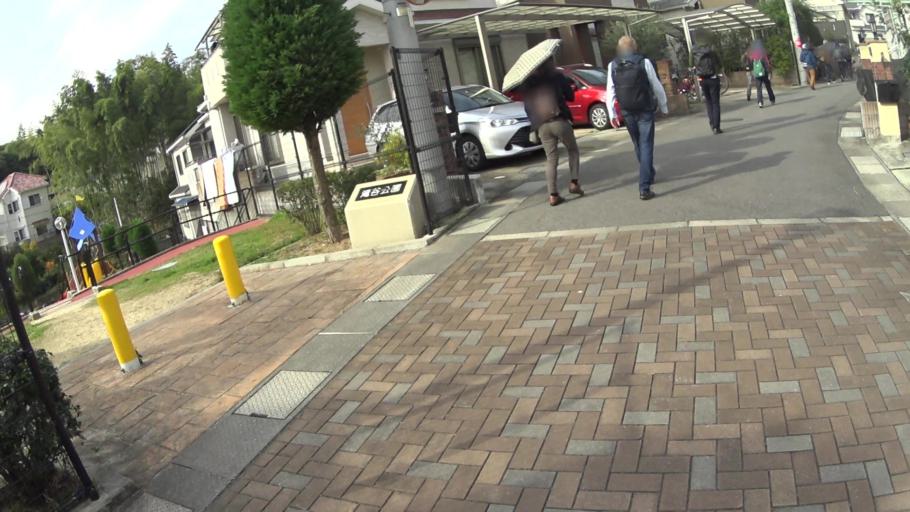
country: JP
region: Kyoto
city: Yawata
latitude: 34.8913
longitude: 135.6684
